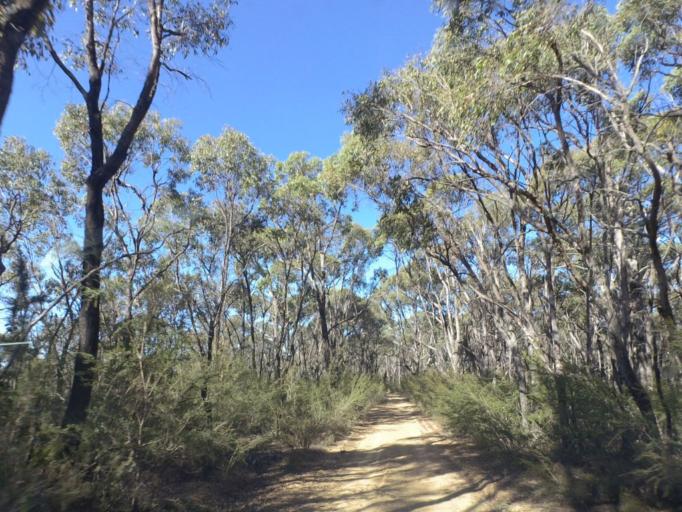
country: AU
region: Victoria
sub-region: Murrindindi
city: Kinglake West
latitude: -37.4719
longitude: 145.3591
